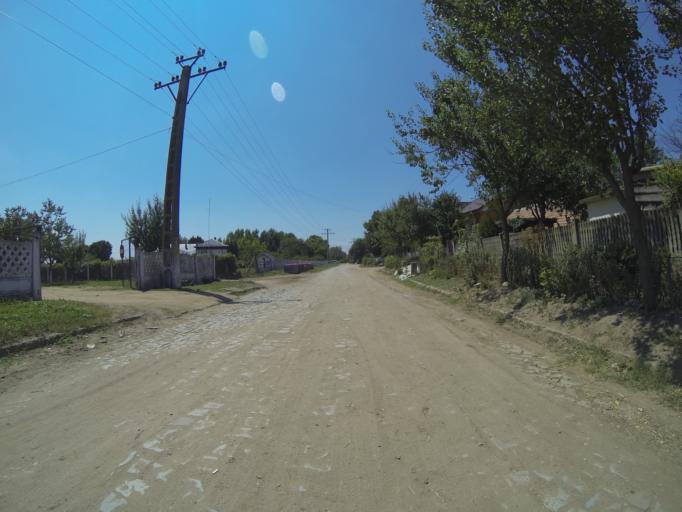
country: RO
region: Dolj
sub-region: Comuna Segarcea
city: Segarcea
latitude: 44.0872
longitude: 23.7492
